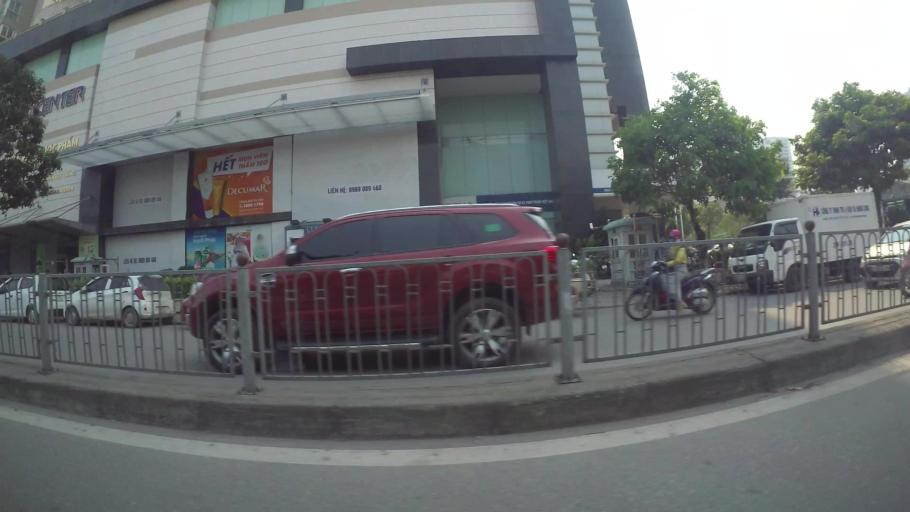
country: VN
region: Ha Noi
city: Thanh Xuan
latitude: 21.0023
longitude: 105.8059
